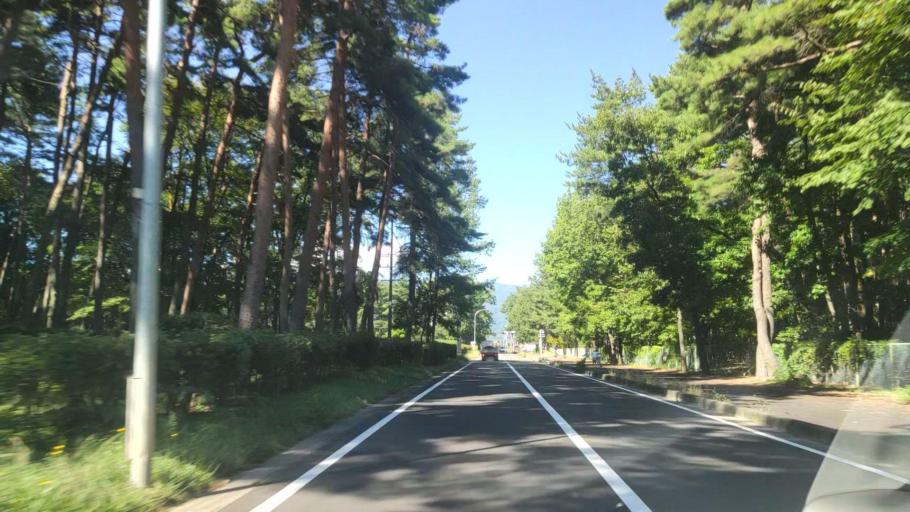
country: JP
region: Nagano
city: Shiojiri
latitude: 36.1629
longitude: 137.9218
